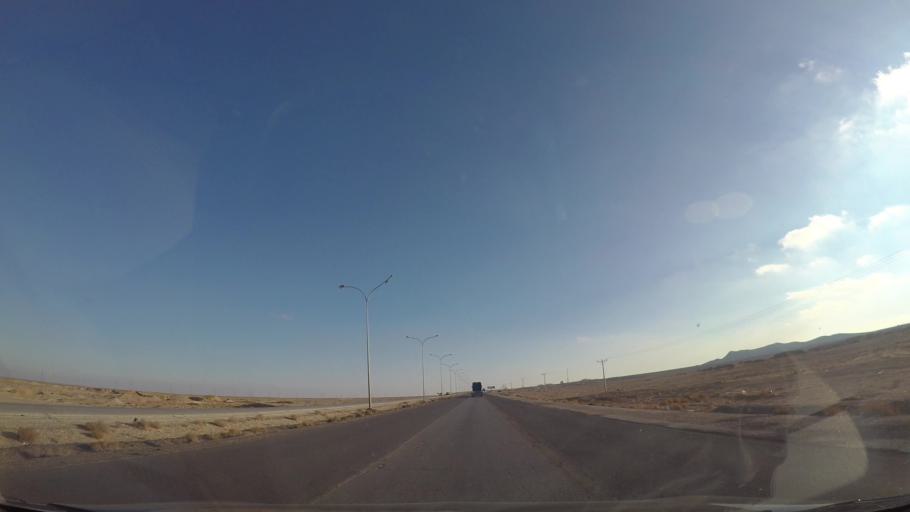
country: JO
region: Tafielah
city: Busayra
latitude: 30.5156
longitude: 35.7995
